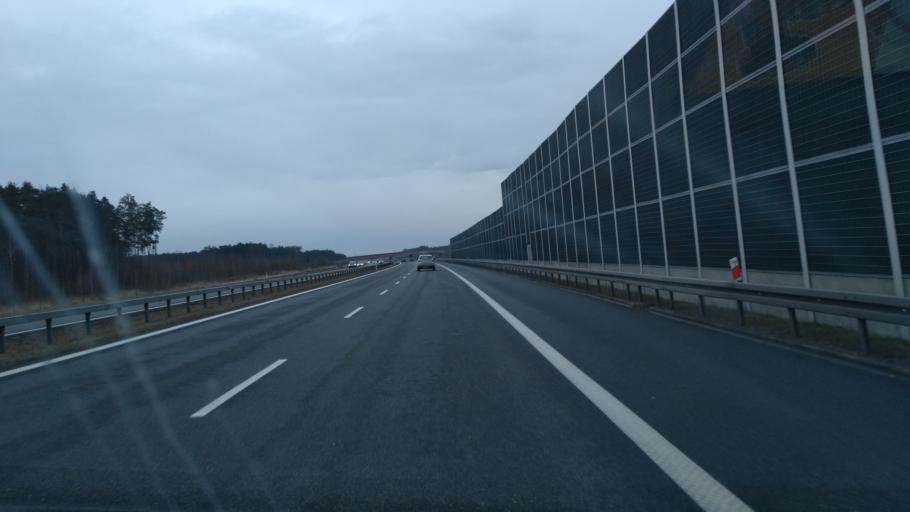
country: PL
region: Lesser Poland Voivodeship
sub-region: Powiat brzeski
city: Debno
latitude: 50.0058
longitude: 20.7737
